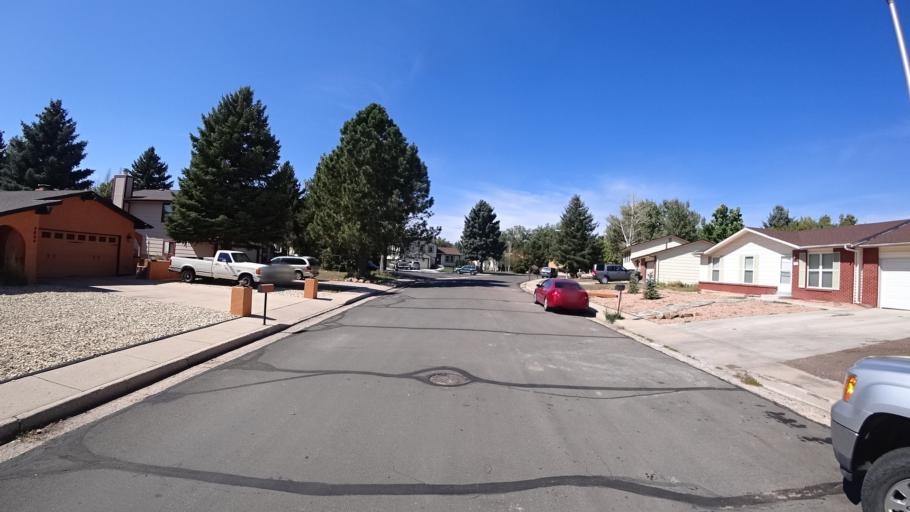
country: US
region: Colorado
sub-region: El Paso County
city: Cimarron Hills
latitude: 38.9026
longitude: -104.7593
